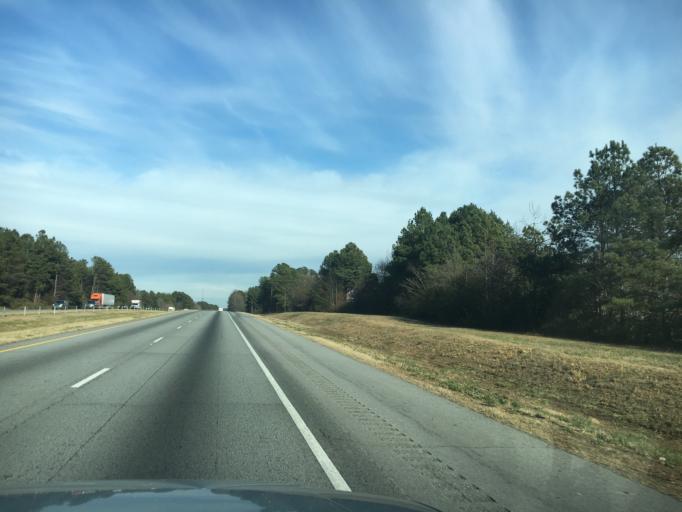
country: US
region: Georgia
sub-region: Franklin County
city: Lavonia
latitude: 34.4554
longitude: -83.1036
